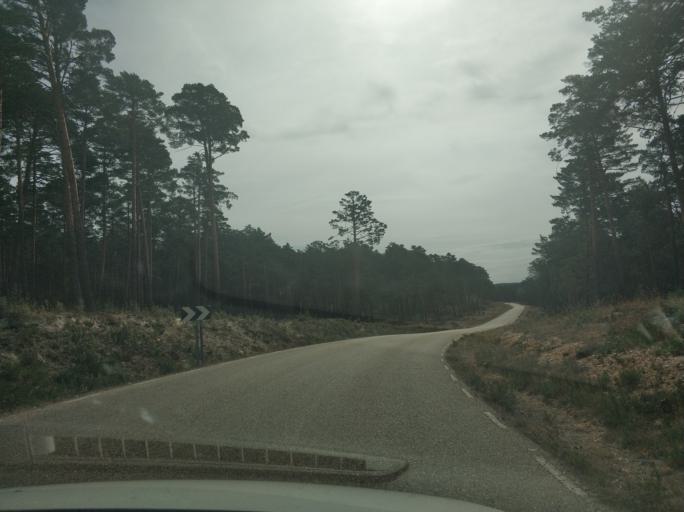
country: ES
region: Castille and Leon
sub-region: Provincia de Soria
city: Navaleno
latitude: 41.8573
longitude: -2.9689
